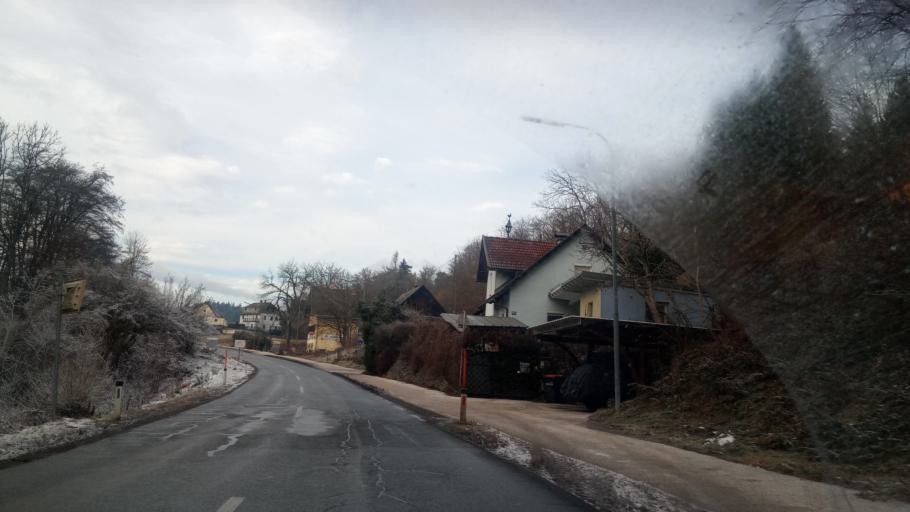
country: AT
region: Carinthia
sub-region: Politischer Bezirk Klagenfurt Land
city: Kottmannsdorf
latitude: 46.5903
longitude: 14.2615
